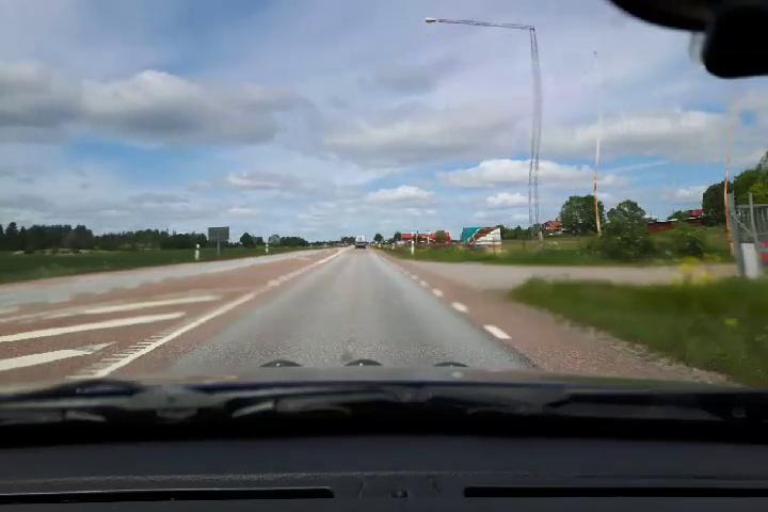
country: SE
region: Uppsala
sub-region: Uppsala Kommun
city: Gamla Uppsala
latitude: 59.9347
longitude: 17.5959
